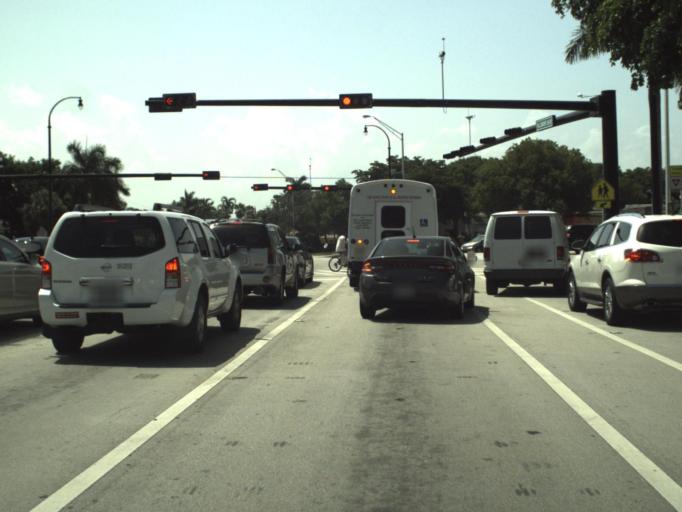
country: US
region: Florida
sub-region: Broward County
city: Deerfield Beach
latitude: 26.3178
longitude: -80.0903
